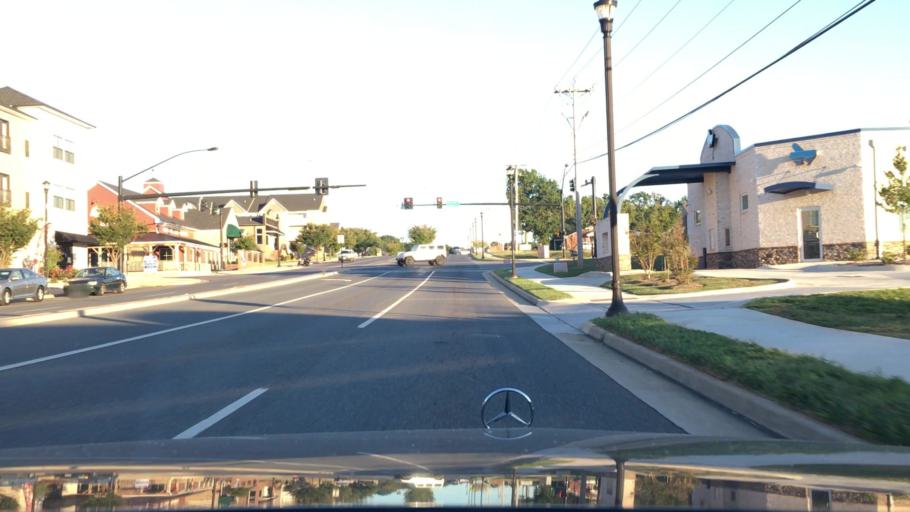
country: US
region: Virginia
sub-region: Campbell County
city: Timberlake
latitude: 37.3396
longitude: -79.2261
